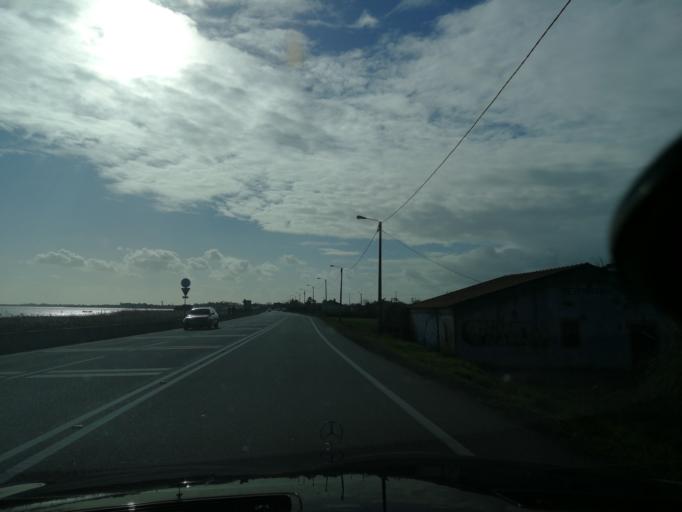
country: PT
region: Aveiro
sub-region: Estarreja
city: Pardilho
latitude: 40.7879
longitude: -8.6807
